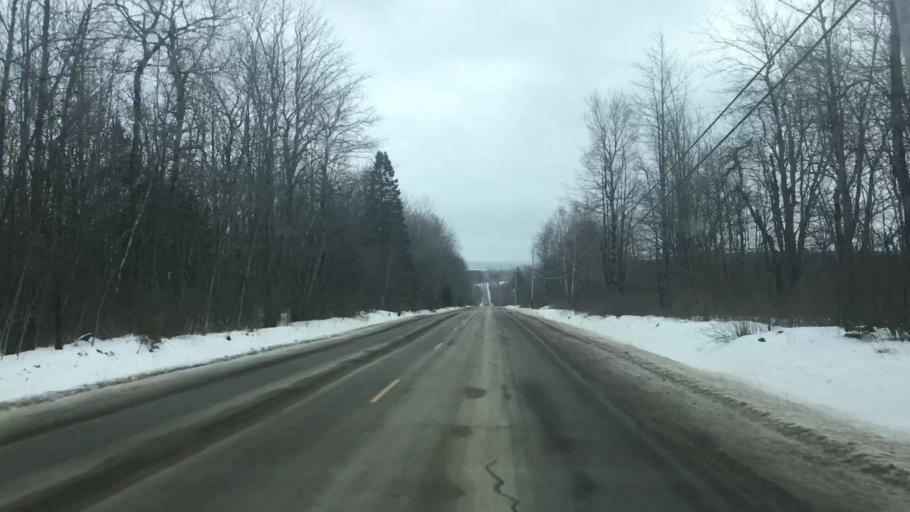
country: US
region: Maine
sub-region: Washington County
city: East Machias
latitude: 44.9749
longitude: -67.4503
